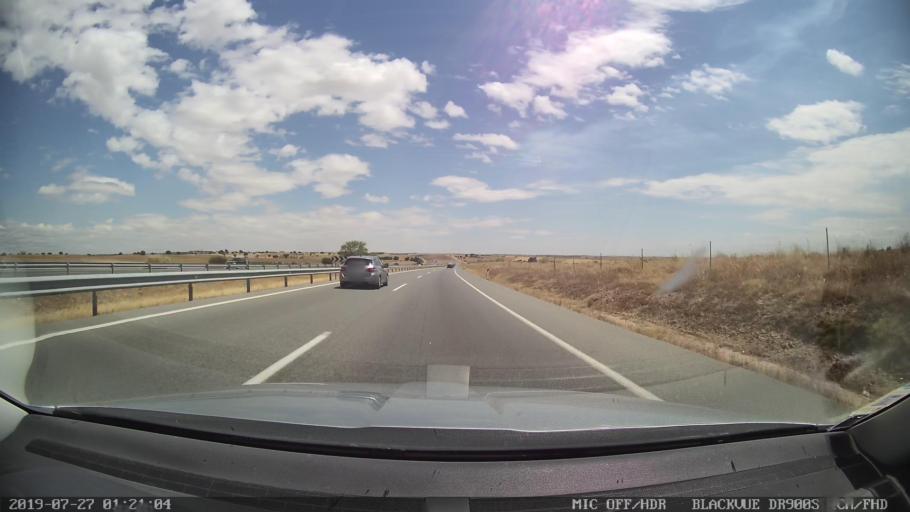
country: ES
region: Castille-La Mancha
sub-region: Province of Toledo
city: Quismondo
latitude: 40.1174
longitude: -4.2889
